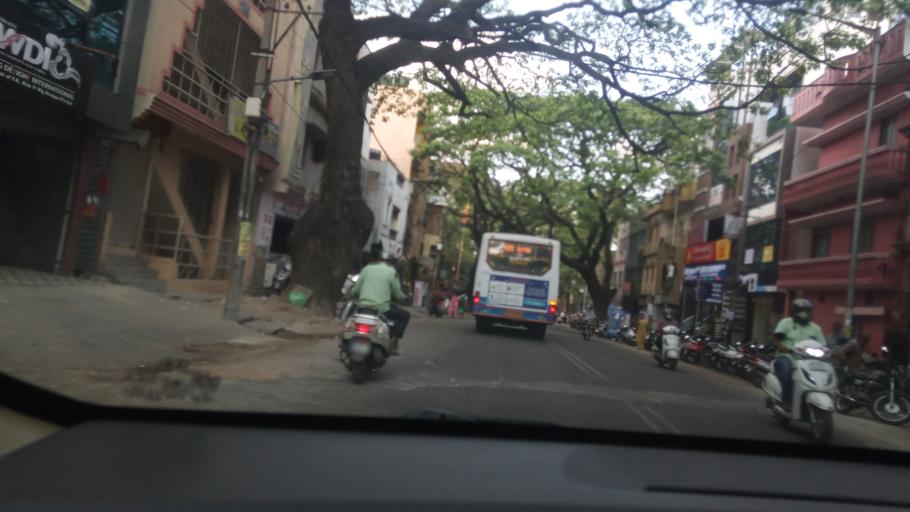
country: IN
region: Karnataka
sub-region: Bangalore Urban
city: Bangalore
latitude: 12.9951
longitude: 77.5520
